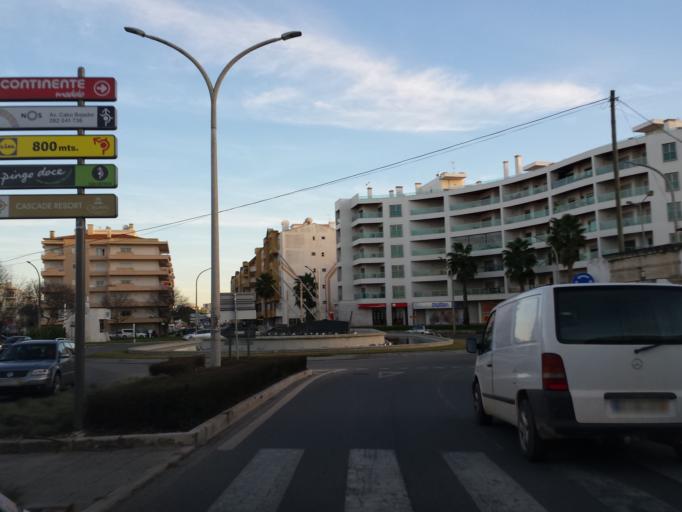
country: PT
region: Faro
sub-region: Lagos
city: Lagos
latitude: 37.1118
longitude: -8.6814
